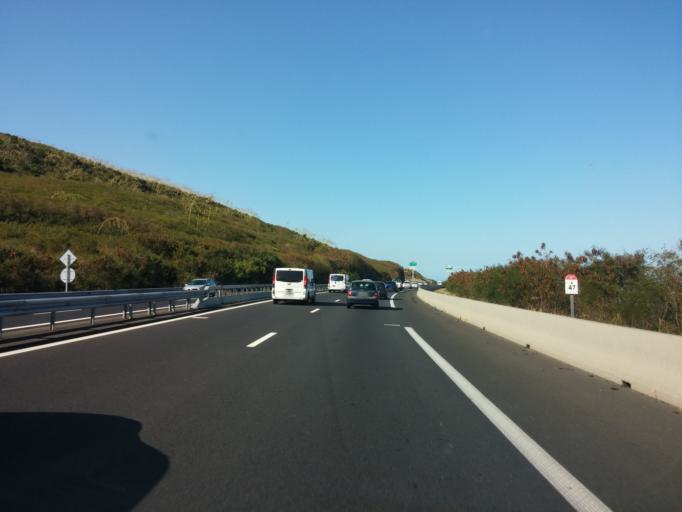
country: RE
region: Reunion
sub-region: Reunion
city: Saint-Leu
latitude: -21.1343
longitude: 55.2849
